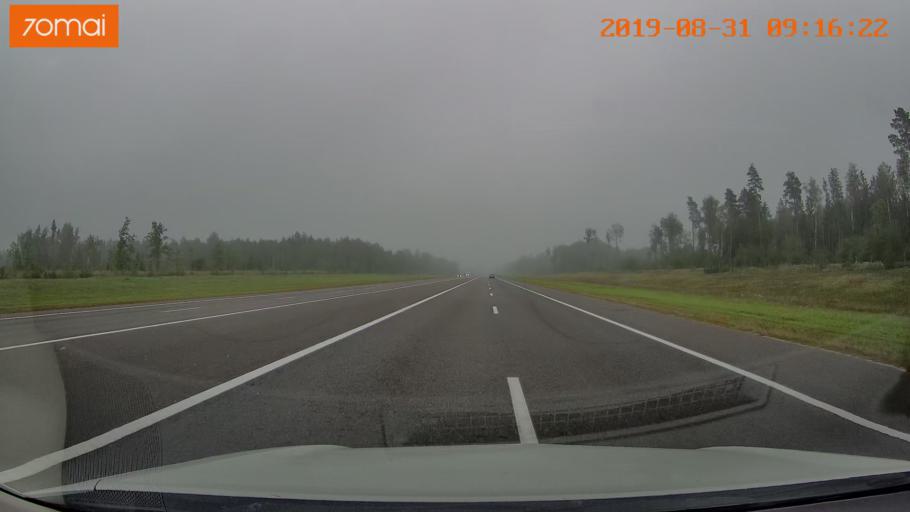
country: BY
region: Minsk
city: Chervyen'
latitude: 53.7715
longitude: 28.7071
